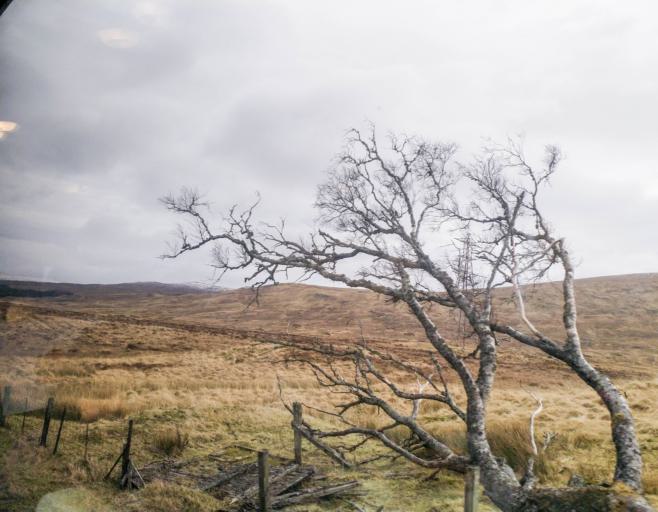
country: GB
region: Scotland
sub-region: Highland
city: Spean Bridge
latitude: 56.5957
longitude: -4.6169
